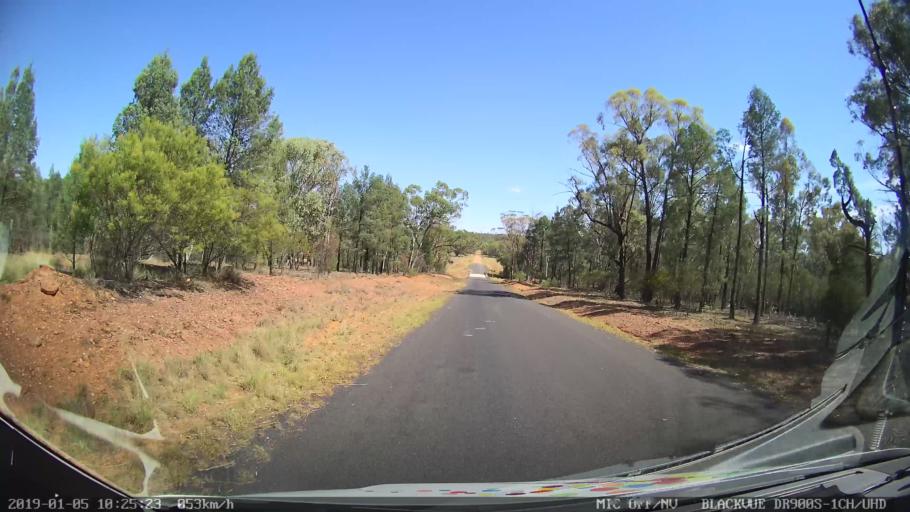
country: AU
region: New South Wales
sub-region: Gilgandra
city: Gilgandra
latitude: -31.5618
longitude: 148.9597
